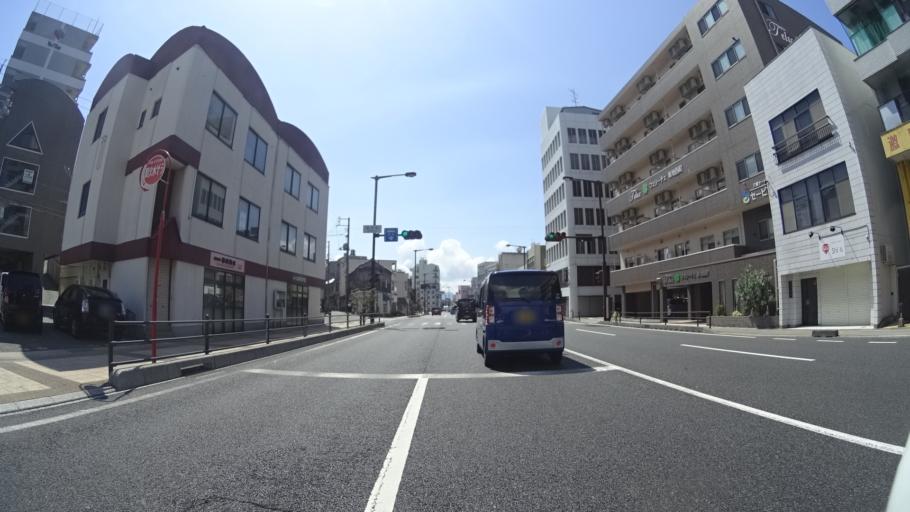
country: JP
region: Yamaguchi
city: Shimonoseki
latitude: 33.9557
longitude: 130.9206
